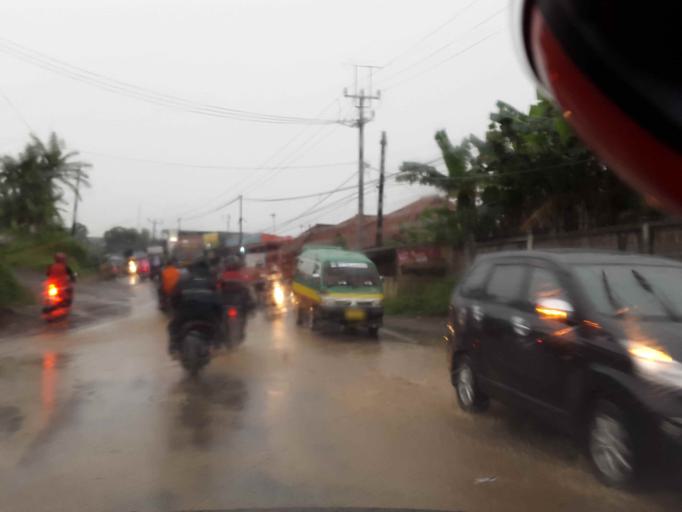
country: ID
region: West Java
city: Cimahi
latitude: -6.9033
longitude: 107.5022
